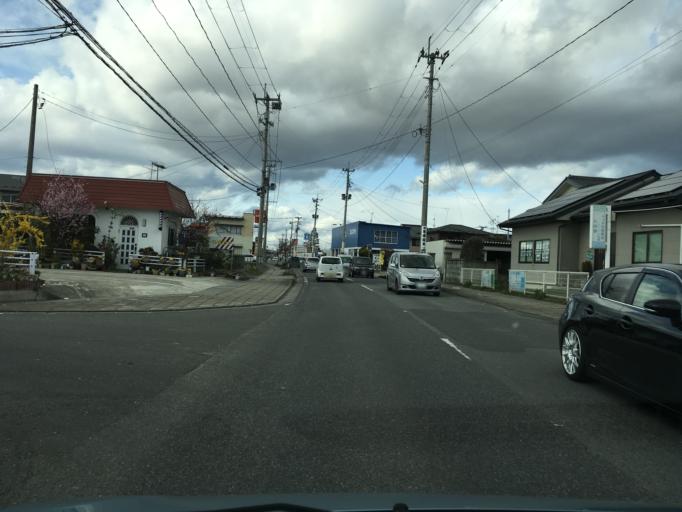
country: JP
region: Miyagi
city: Wakuya
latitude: 38.6781
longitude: 141.1944
